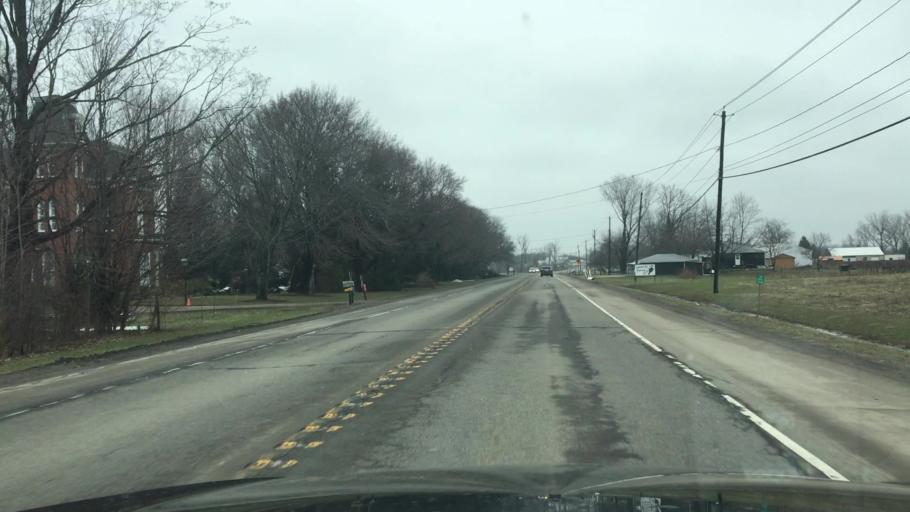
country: US
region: New York
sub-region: Chautauqua County
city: Fredonia
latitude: 42.4267
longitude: -79.3063
